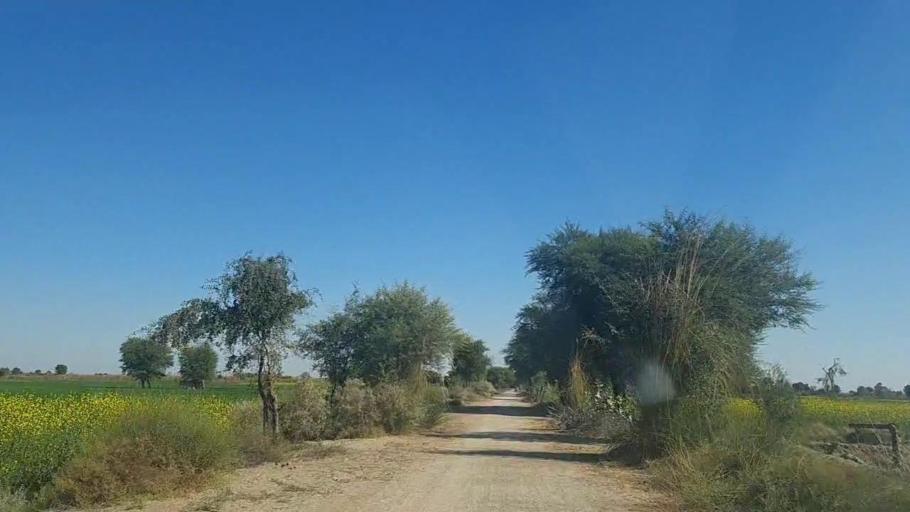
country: PK
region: Sindh
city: Khadro
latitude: 26.2180
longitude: 68.8653
